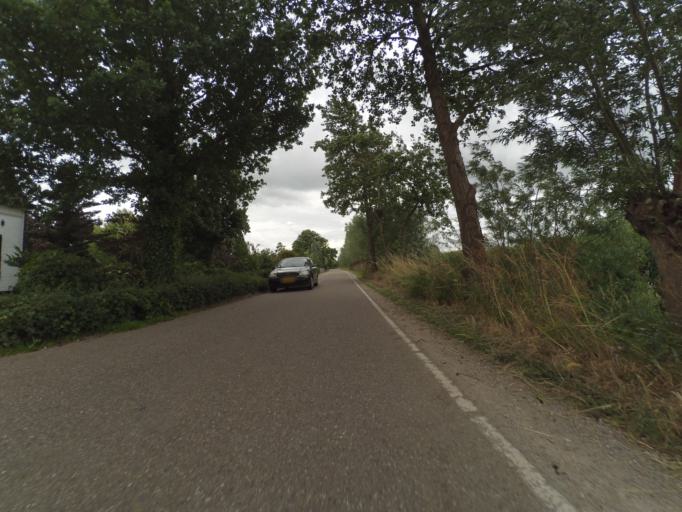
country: NL
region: South Holland
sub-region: Gemeente Giessenlanden
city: Giessenburg
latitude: 51.8558
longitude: 4.9224
